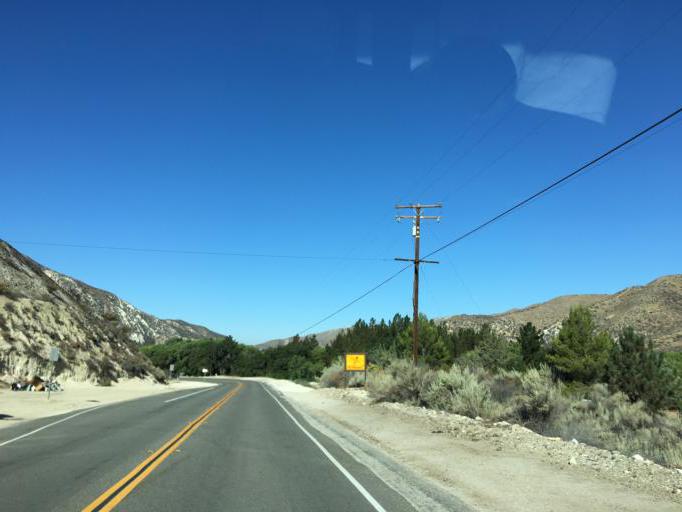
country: US
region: California
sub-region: Los Angeles County
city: Agua Dulce
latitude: 34.4406
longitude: -118.3092
